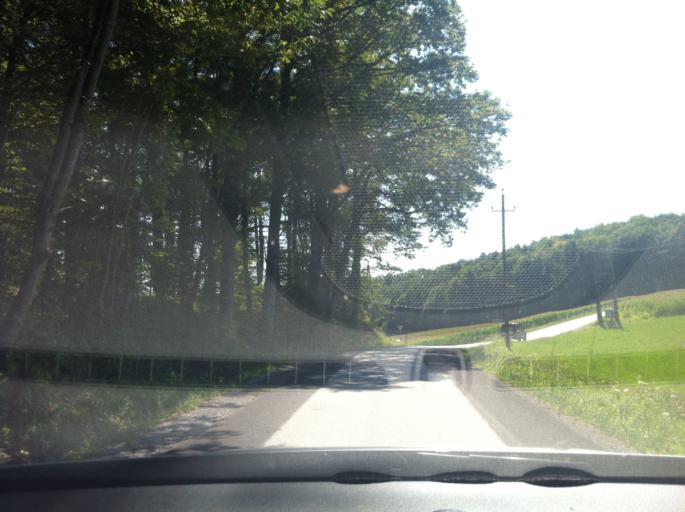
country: AT
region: Styria
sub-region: Politischer Bezirk Weiz
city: Barnbach
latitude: 47.0304
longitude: 15.8445
